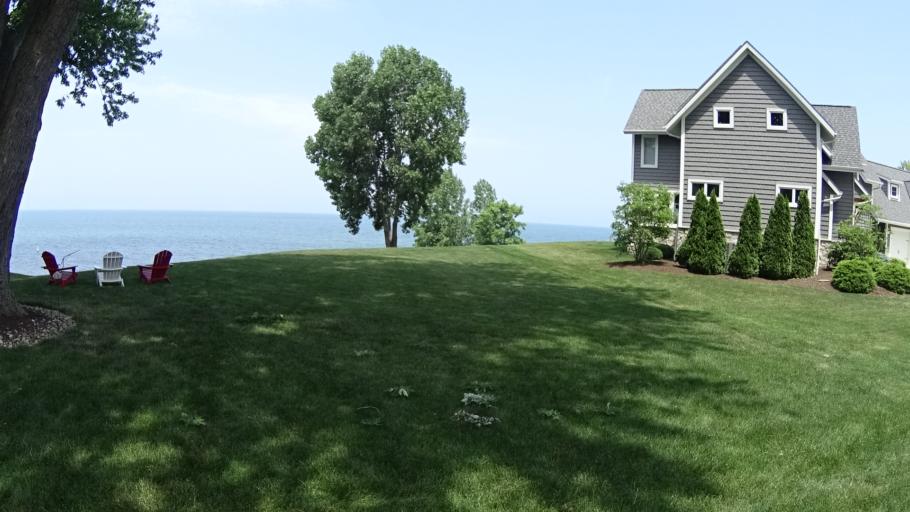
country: US
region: Ohio
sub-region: Lorain County
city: Vermilion
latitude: 41.4062
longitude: -82.4108
